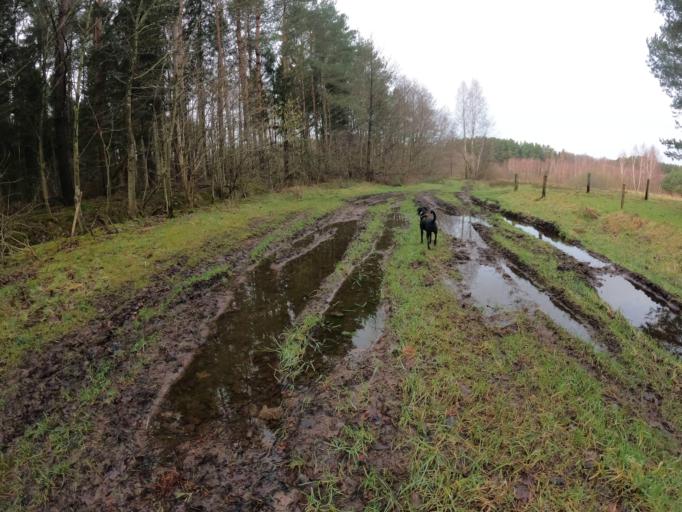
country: PL
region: West Pomeranian Voivodeship
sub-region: Powiat slawienski
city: Darlowo
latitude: 54.4216
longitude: 16.4966
